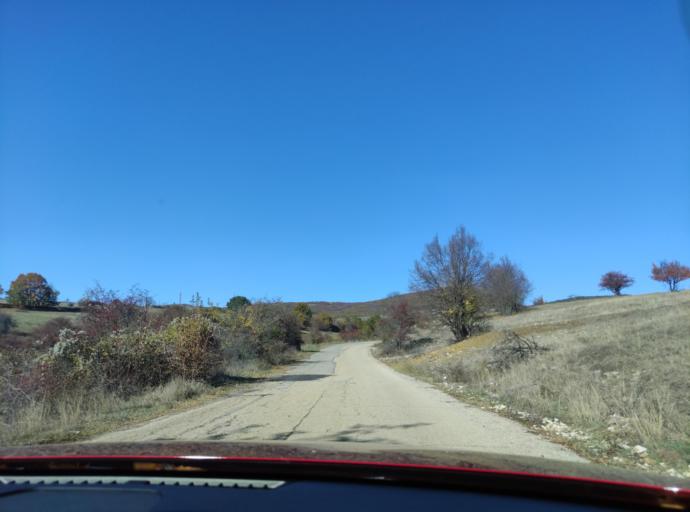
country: BG
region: Montana
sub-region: Obshtina Montana
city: Montana
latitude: 43.4430
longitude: 23.0494
